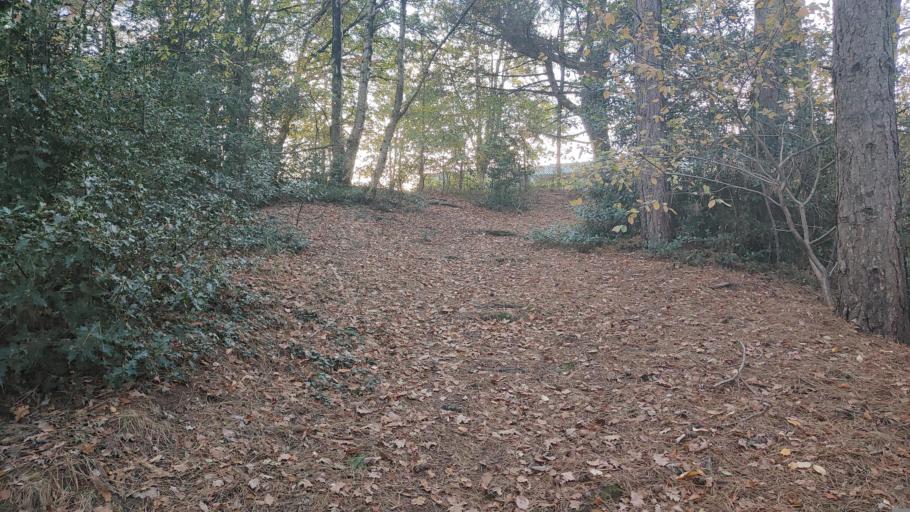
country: BE
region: Wallonia
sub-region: Province de Liege
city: La Calamine
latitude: 50.7234
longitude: 6.0194
